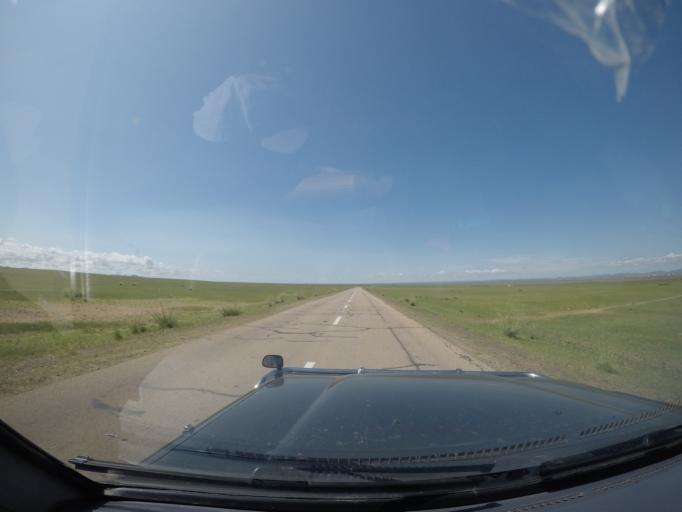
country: MN
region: Hentiy
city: Undurkhaan
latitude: 47.2775
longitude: 110.7418
